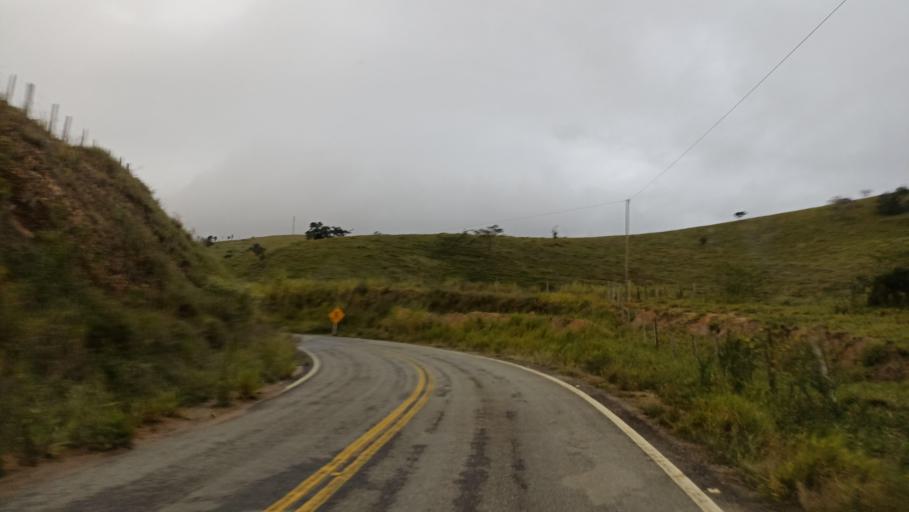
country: BR
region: Minas Gerais
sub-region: Joaima
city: Joaima
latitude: -16.6732
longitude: -40.5289
